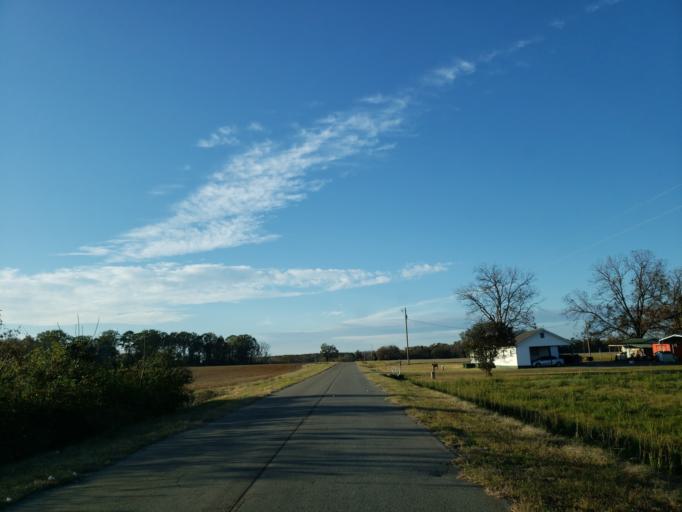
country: US
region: Georgia
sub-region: Dooly County
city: Unadilla
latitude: 32.2087
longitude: -83.7753
